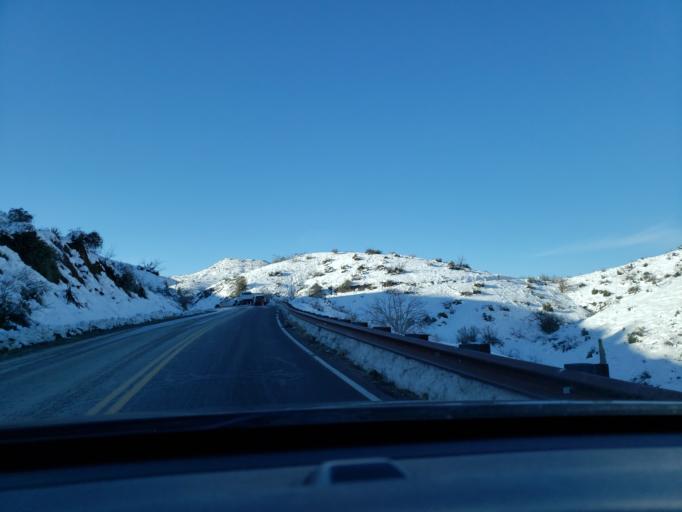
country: US
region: Arizona
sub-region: Maricopa County
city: Carefree
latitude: 33.8998
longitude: -111.8241
